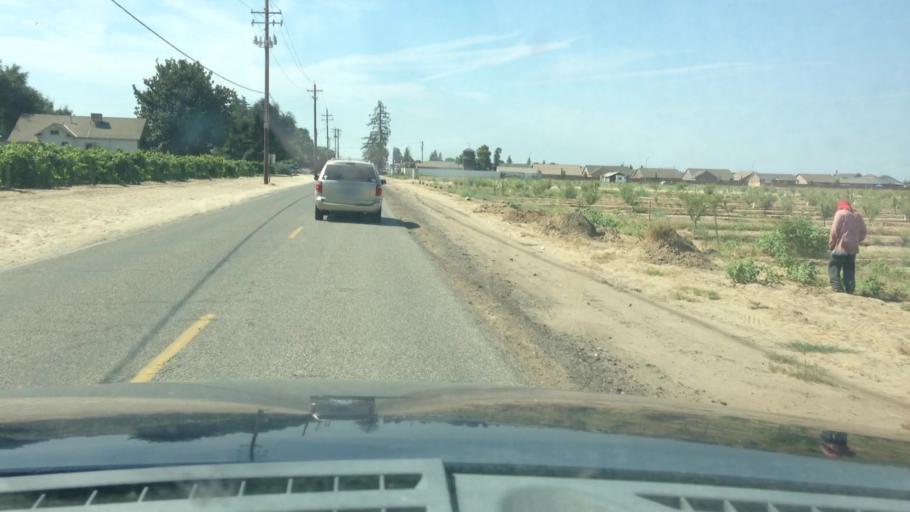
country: US
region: California
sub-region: Fresno County
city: Kingsburg
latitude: 36.5355
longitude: -119.5567
